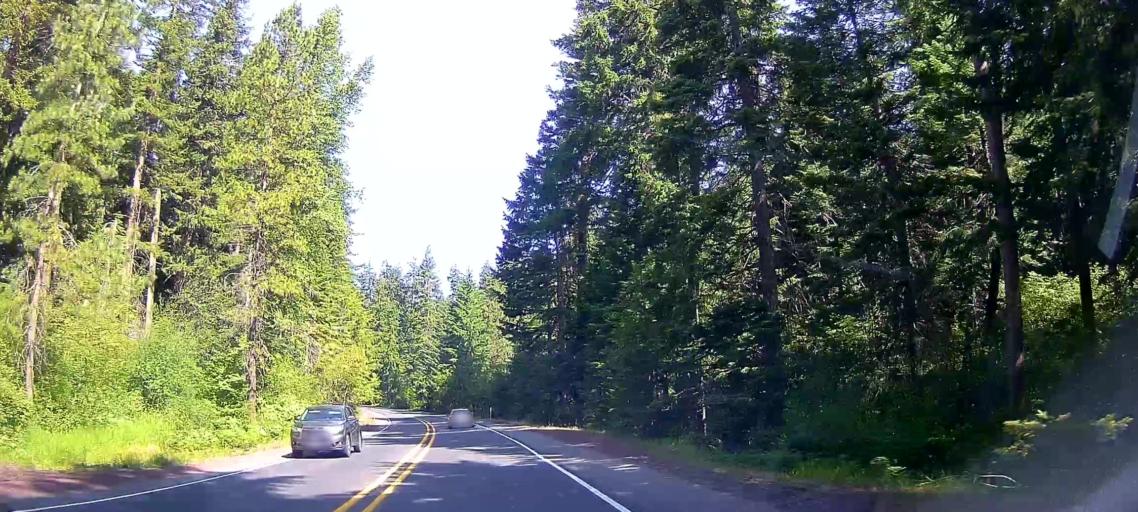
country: US
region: Oregon
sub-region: Jefferson County
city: Warm Springs
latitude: 45.1070
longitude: -121.5583
